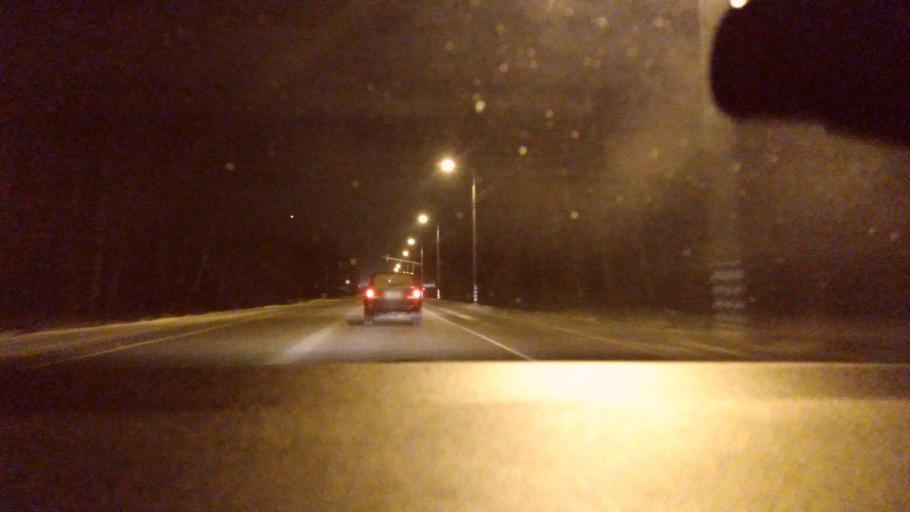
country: RU
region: Moskovskaya
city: Il'inskiy Pogost
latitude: 55.4881
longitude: 38.8961
